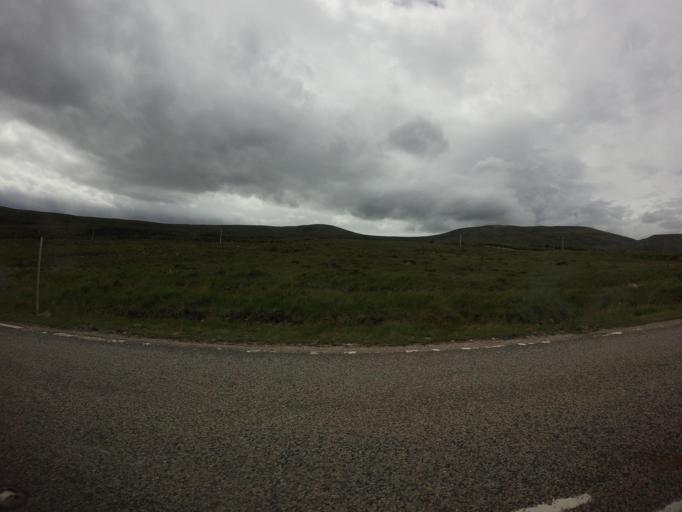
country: GB
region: Scotland
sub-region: Highland
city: Ullapool
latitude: 57.7082
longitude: -4.8325
